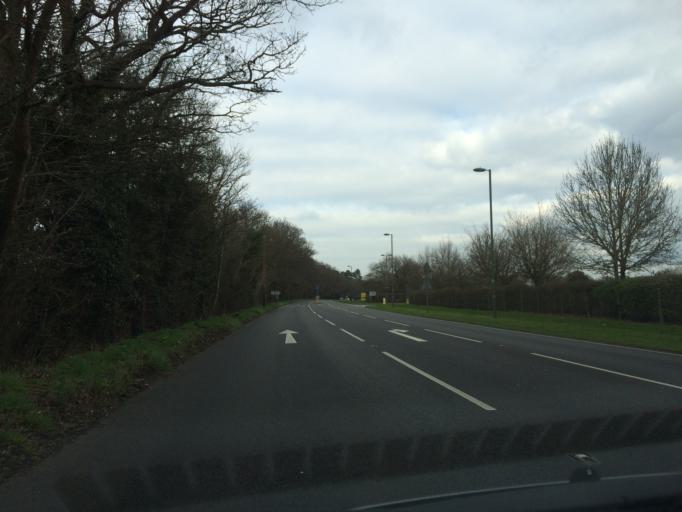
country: GB
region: England
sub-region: Surrey
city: Woking
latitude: 51.3521
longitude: -0.5629
